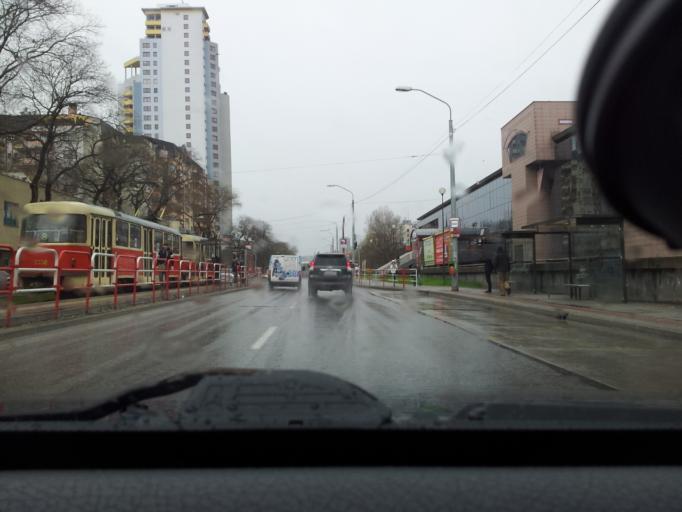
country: SK
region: Bratislavsky
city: Bratislava
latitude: 48.1559
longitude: 17.1414
